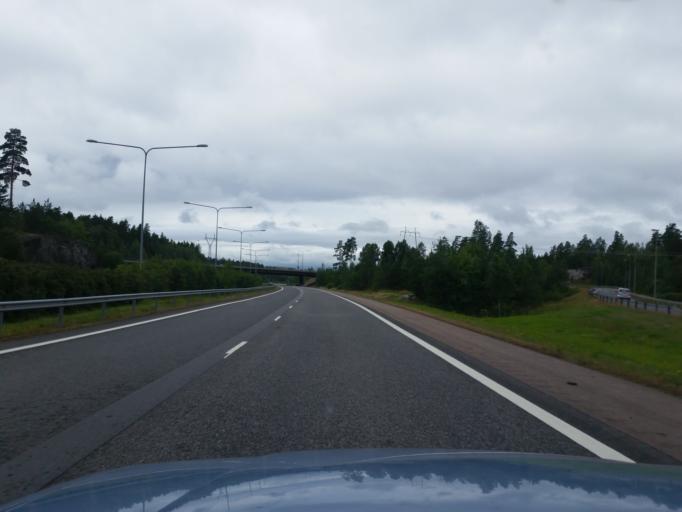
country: FI
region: Varsinais-Suomi
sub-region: Turku
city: Piikkioe
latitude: 60.4445
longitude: 22.4965
